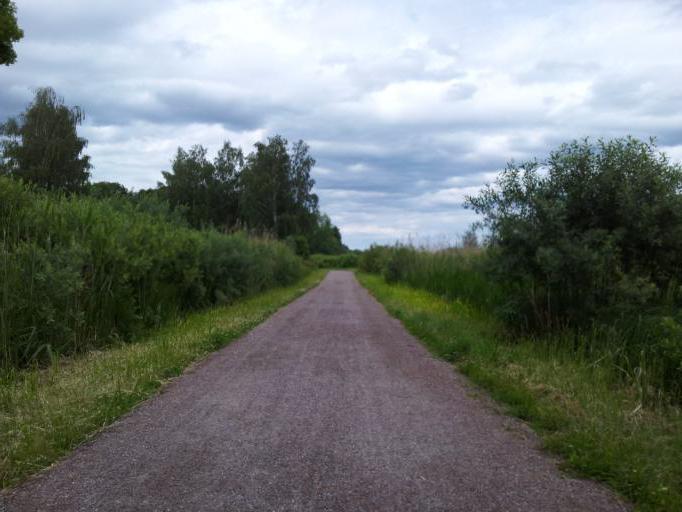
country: SE
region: Uppsala
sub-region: Uppsala Kommun
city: Saevja
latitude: 59.8035
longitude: 17.6638
